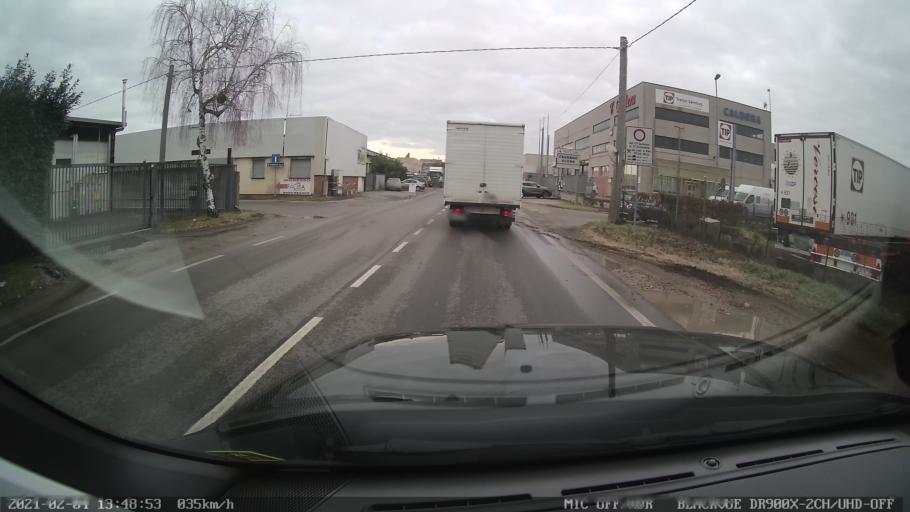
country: IT
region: Lombardy
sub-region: Provincia di Varese
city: Solbiate Olona
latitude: 45.6559
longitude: 8.8694
